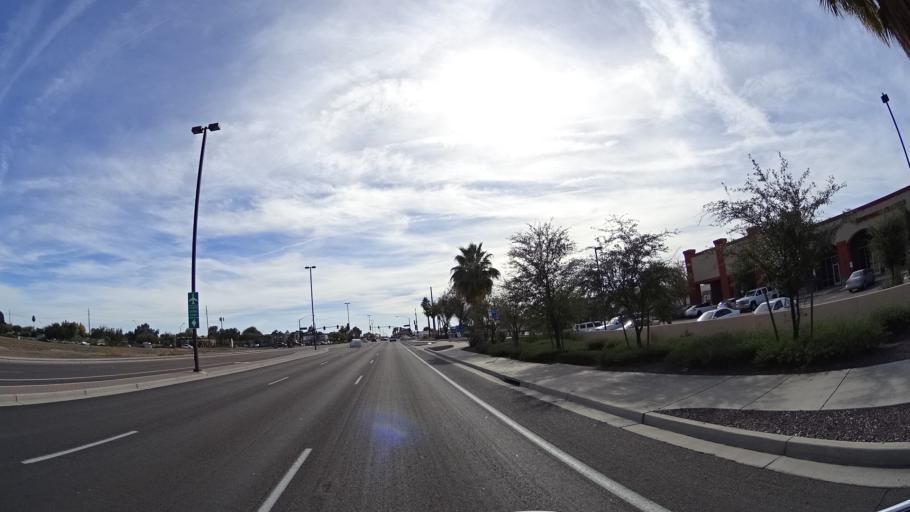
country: US
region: Arizona
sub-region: Maricopa County
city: Gilbert
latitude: 33.3225
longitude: -111.7899
